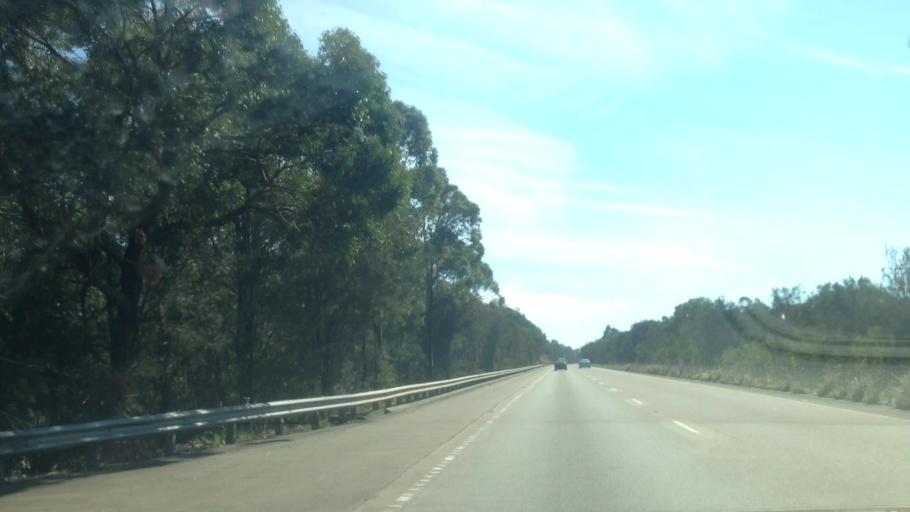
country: AU
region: New South Wales
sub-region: Lake Macquarie Shire
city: Fennell Bay
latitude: -32.9661
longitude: 151.5366
